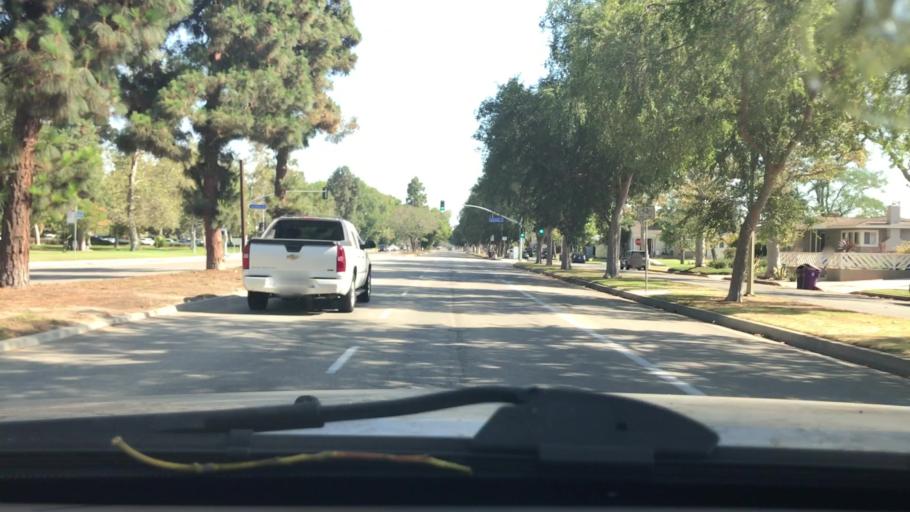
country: US
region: California
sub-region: Orange County
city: Rossmoor
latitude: 33.8008
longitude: -118.0993
